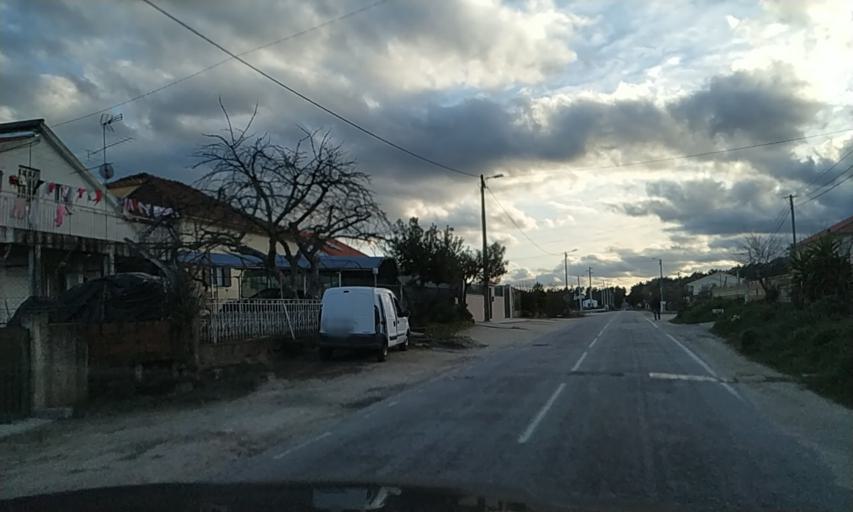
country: PT
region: Braganca
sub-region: Carrazeda de Ansiaes
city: Carrazeda de Anciaes
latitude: 41.2972
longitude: -7.3439
